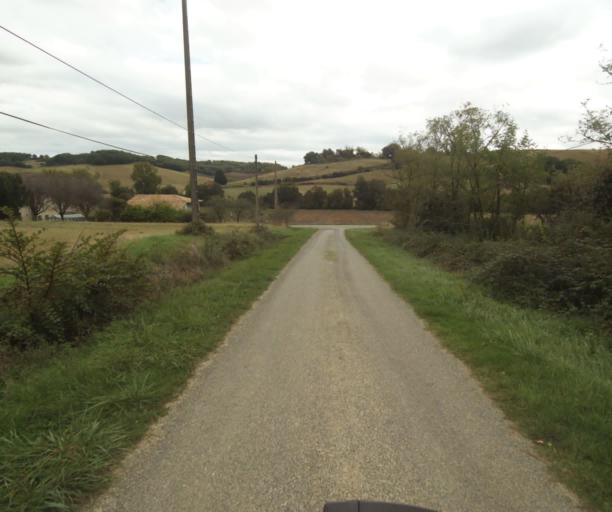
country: FR
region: Midi-Pyrenees
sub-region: Departement du Tarn-et-Garonne
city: Beaumont-de-Lomagne
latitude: 43.8514
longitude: 1.0823
